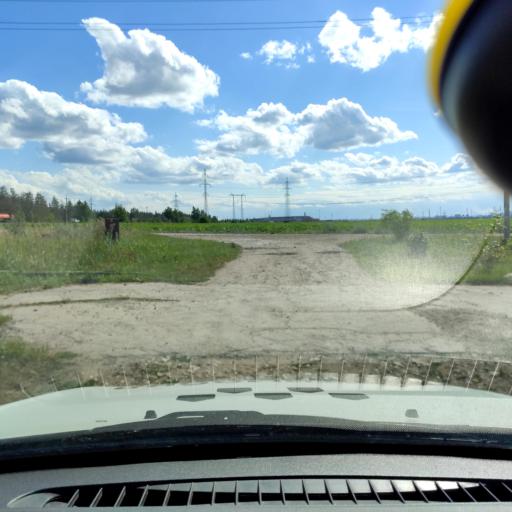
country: RU
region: Samara
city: Zhigulevsk
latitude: 53.5804
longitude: 49.5624
